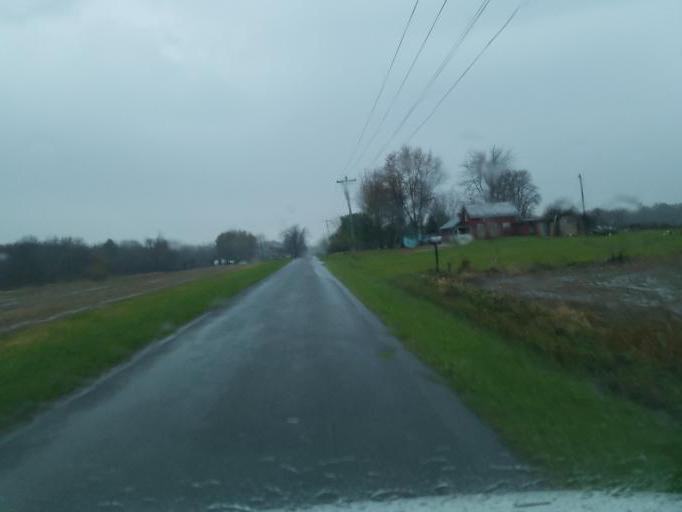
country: US
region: Ohio
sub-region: Delaware County
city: Ashley
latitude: 40.4197
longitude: -82.8993
